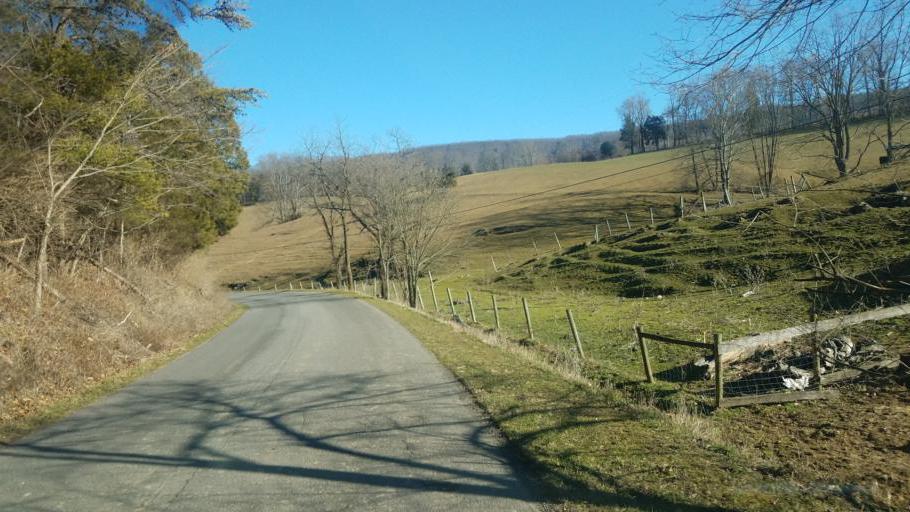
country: US
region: Virginia
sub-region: Pulaski County
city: Pulaski
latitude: 37.1834
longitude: -80.8405
